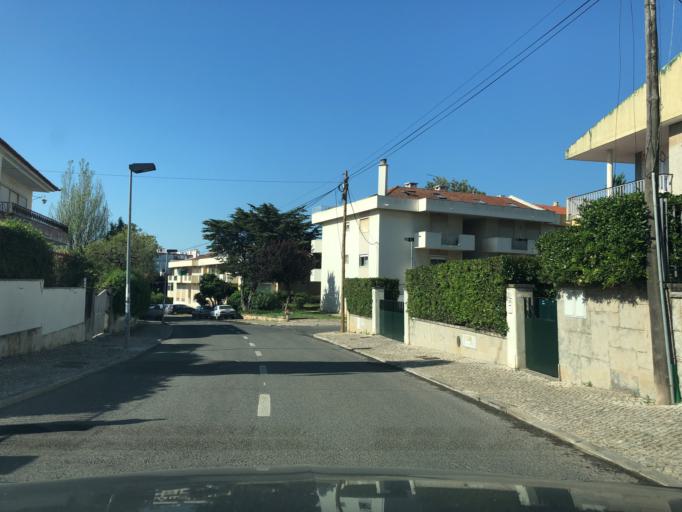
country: PT
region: Lisbon
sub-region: Oeiras
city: Paco de Arcos
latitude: 38.6957
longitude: -9.2989
